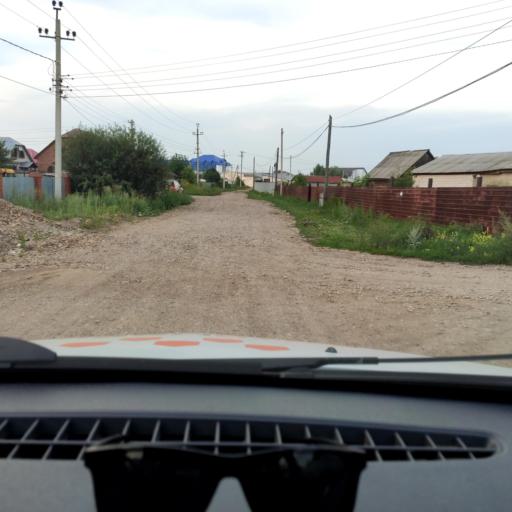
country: RU
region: Bashkortostan
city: Ufa
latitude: 54.6117
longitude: 55.9315
